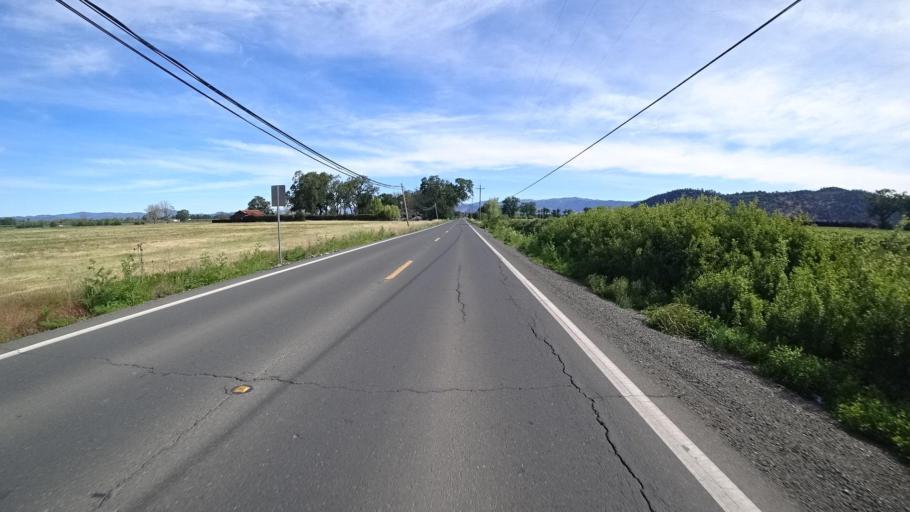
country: US
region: California
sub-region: Lake County
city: Kelseyville
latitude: 38.9857
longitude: -122.8291
